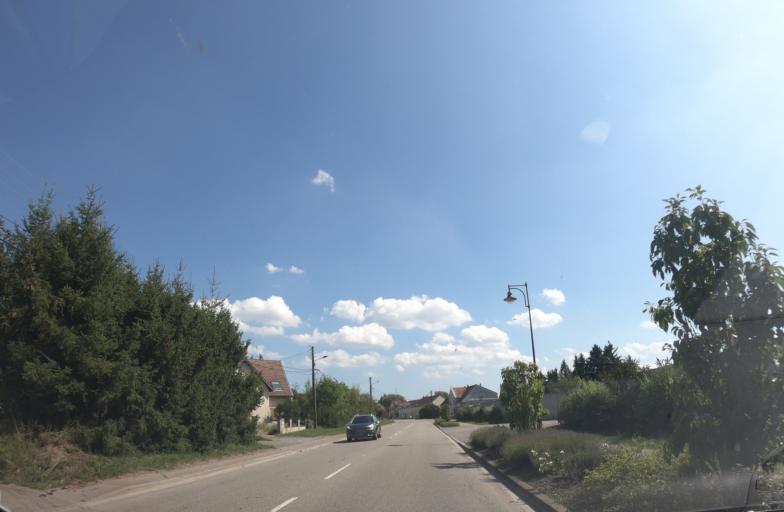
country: FR
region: Lorraine
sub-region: Departement de la Moselle
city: Diebling
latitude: 49.1118
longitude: 6.9339
